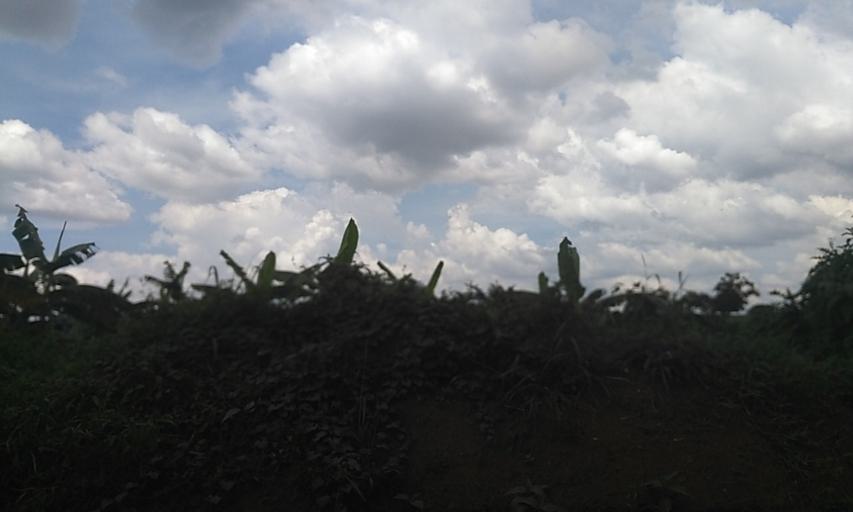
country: UG
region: Central Region
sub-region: Wakiso District
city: Wakiso
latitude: 0.3524
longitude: 32.4714
